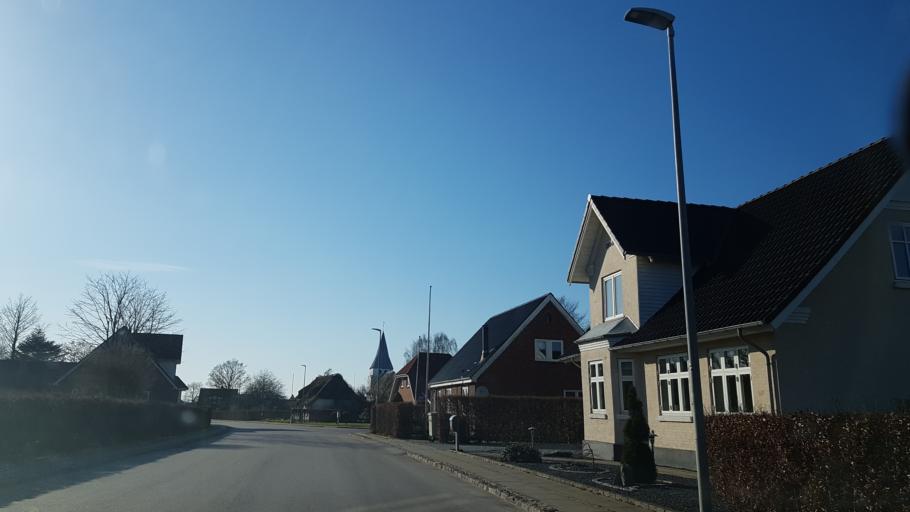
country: DK
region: South Denmark
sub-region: Vejen Kommune
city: Brorup
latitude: 55.4089
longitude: 8.9780
